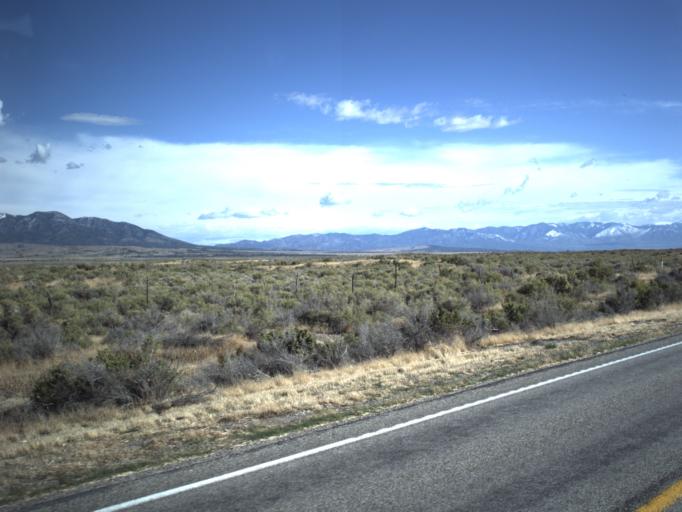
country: US
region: Utah
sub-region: Millard County
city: Delta
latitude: 39.3128
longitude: -112.4780
